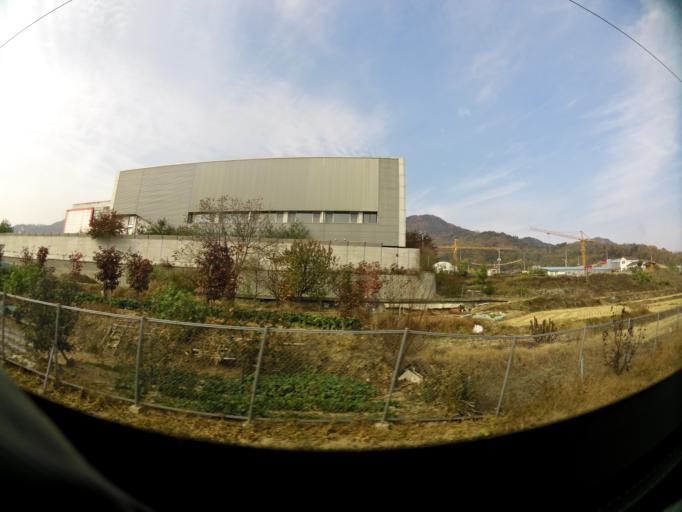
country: KR
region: Gyeongsangbuk-do
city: Gumi
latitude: 36.0906
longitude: 128.3525
